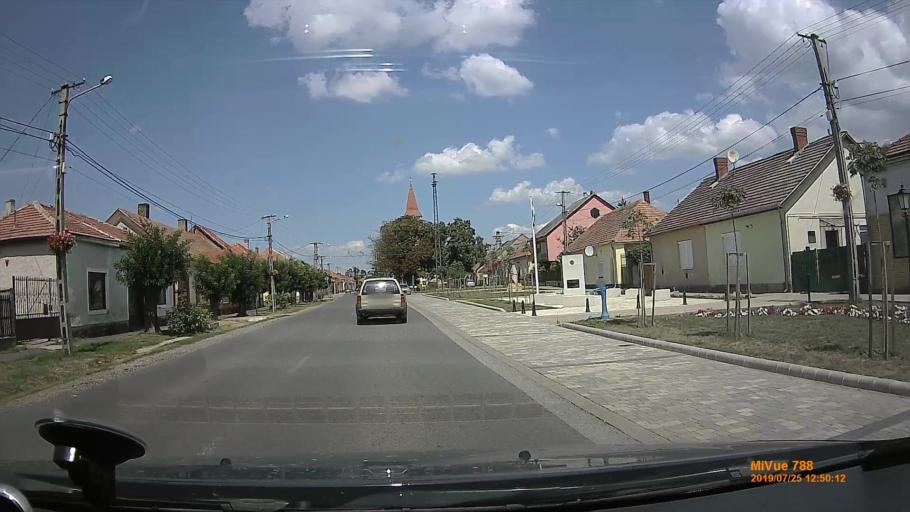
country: HU
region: Borsod-Abauj-Zemplen
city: Abaujszanto
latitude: 48.2788
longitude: 21.1864
